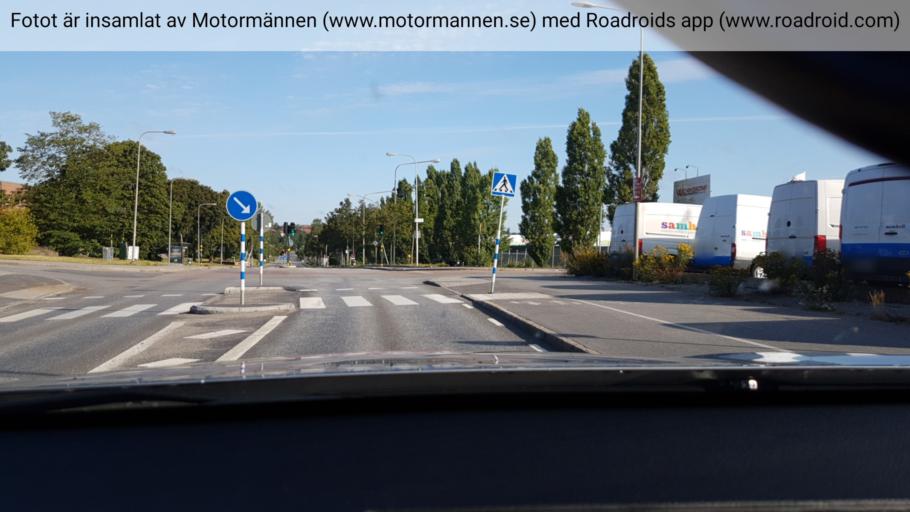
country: SE
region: Stockholm
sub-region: Stockholms Kommun
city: Arsta
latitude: 59.2903
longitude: 18.0186
